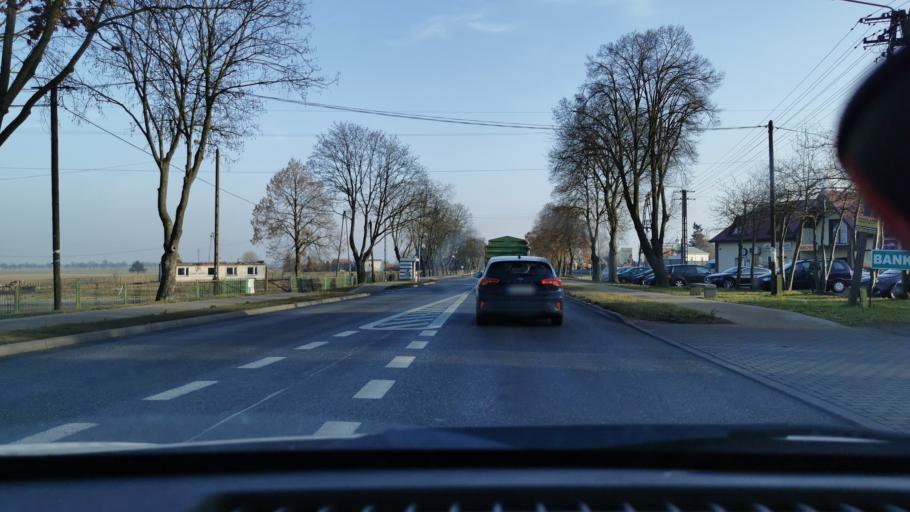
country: PL
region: Lodz Voivodeship
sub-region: Powiat sieradzki
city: Wroblew
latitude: 51.6109
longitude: 18.6183
